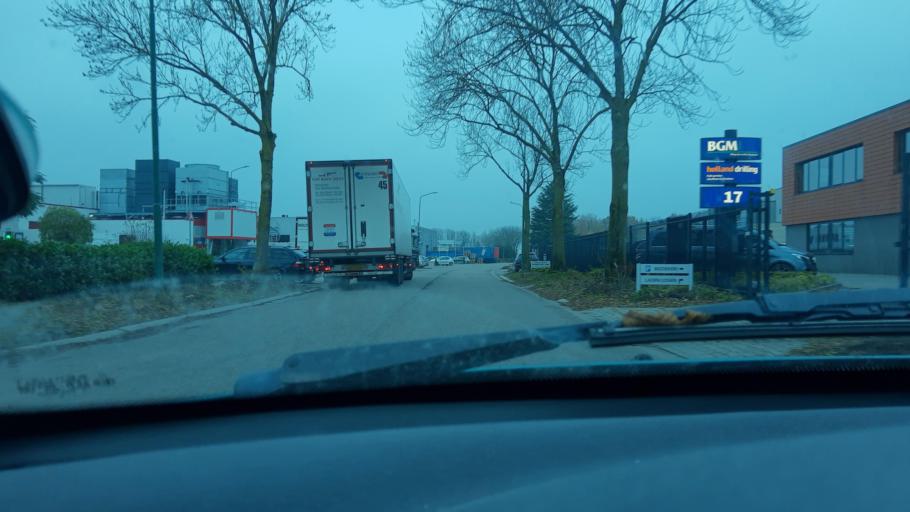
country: NL
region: North Brabant
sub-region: Gemeente Cuijk
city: Cuijk
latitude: 51.7202
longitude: 5.8757
